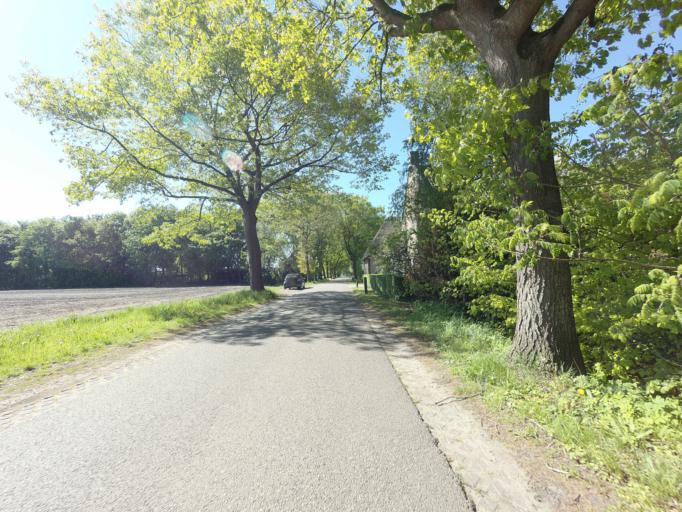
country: NL
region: North Brabant
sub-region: Gemeente Rucphen
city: Rucphen
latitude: 51.5853
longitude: 4.5591
